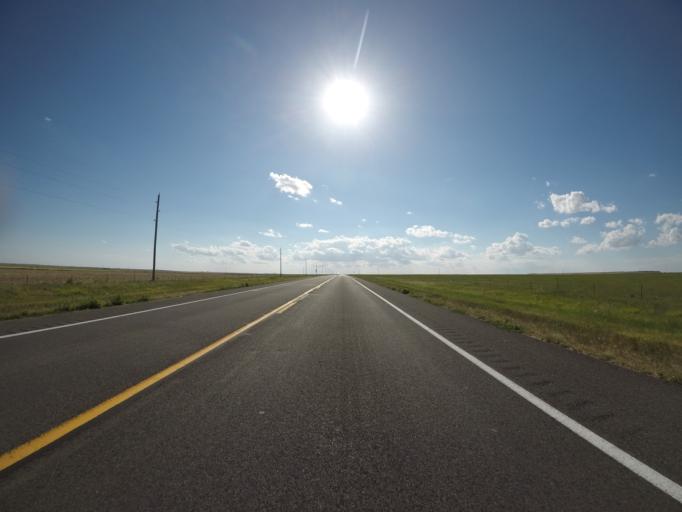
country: US
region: Colorado
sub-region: Morgan County
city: Fort Morgan
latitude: 40.6109
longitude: -103.7682
